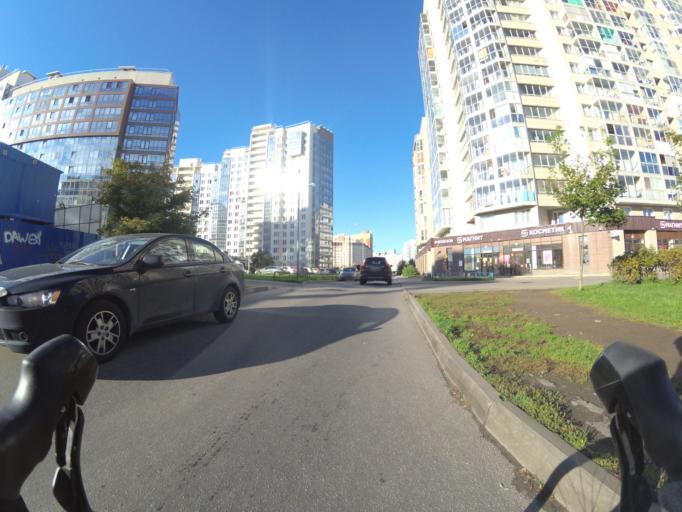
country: RU
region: Leningrad
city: Untolovo
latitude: 60.0000
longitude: 30.2081
